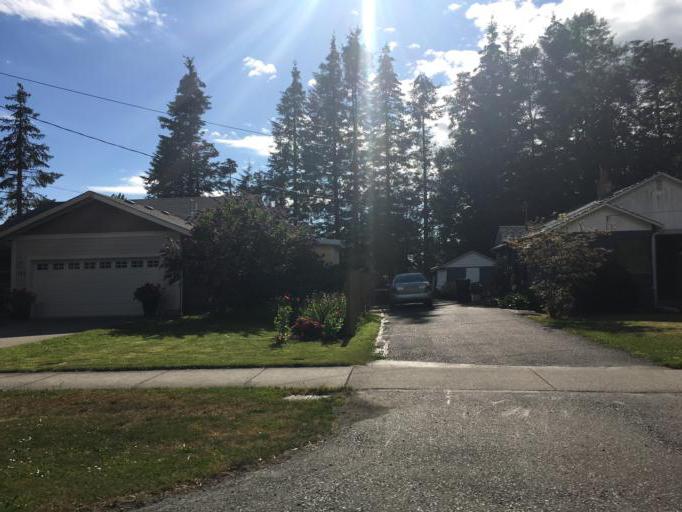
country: US
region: Washington
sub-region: Whatcom County
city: Nooksack
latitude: 48.9239
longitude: -122.3220
